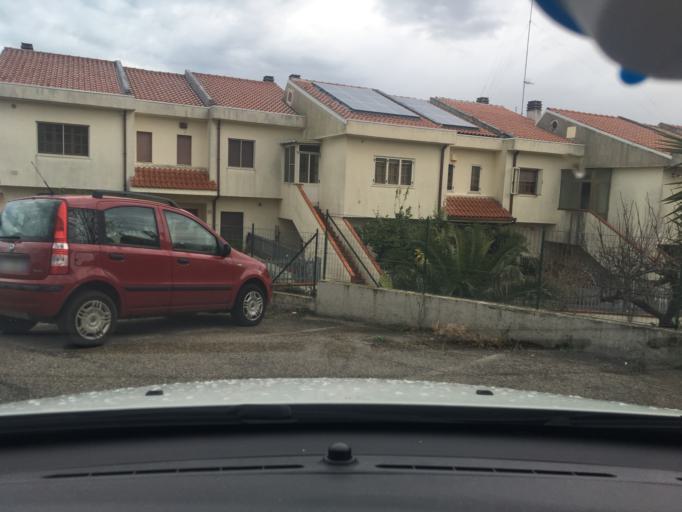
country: IT
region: Molise
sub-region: Provincia di Campobasso
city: Termoli
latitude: 41.9732
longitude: 14.9962
